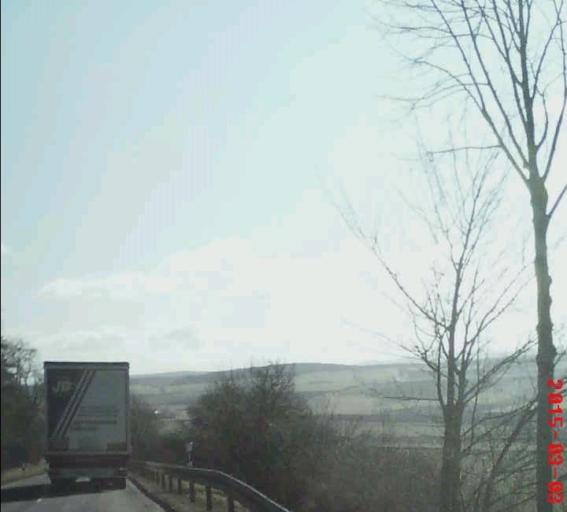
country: DE
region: Thuringia
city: Stadtilm
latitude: 50.7640
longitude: 11.1203
